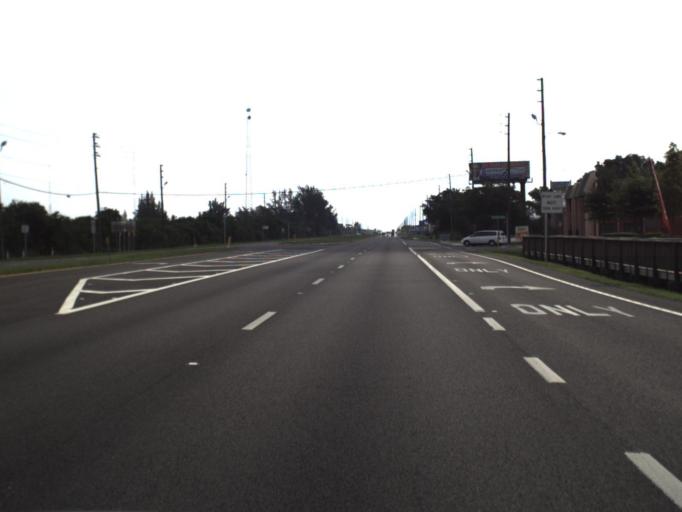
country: US
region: Florida
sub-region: Pinellas County
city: Gandy
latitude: 27.8681
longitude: -82.6229
